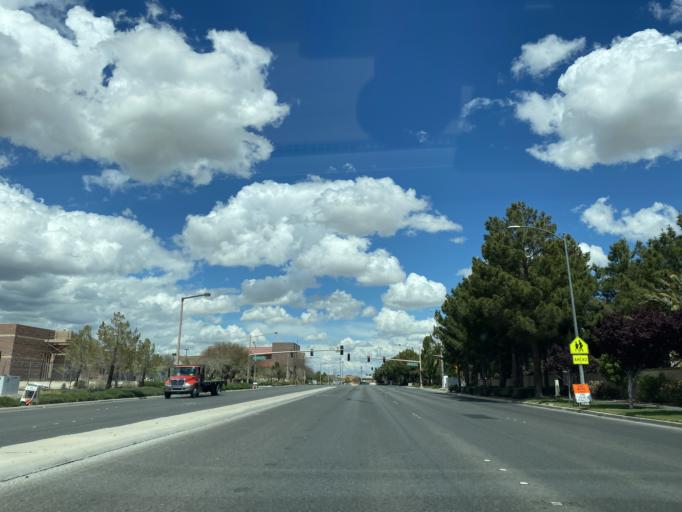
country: US
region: Nevada
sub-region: Clark County
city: Summerlin South
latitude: 36.1513
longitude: -115.3156
